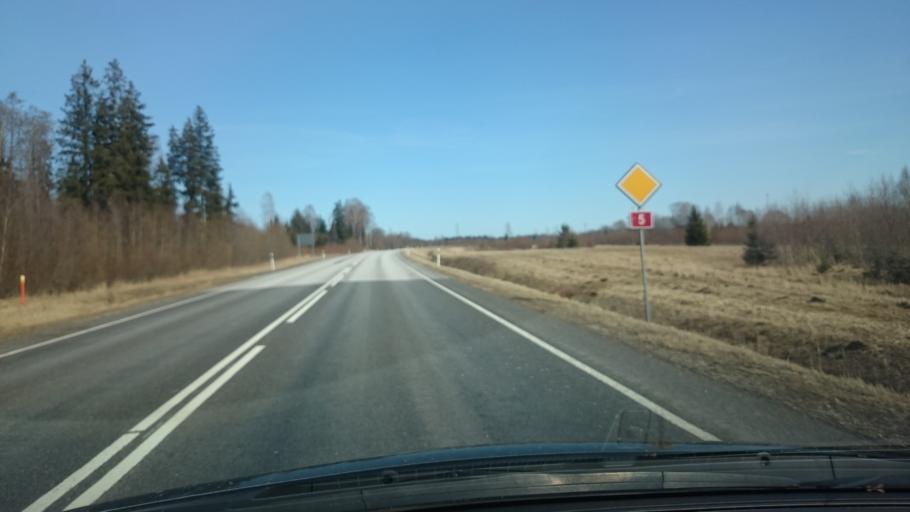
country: EE
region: Paernumaa
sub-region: Vaendra vald (alev)
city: Vandra
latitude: 58.6550
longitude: 25.0022
